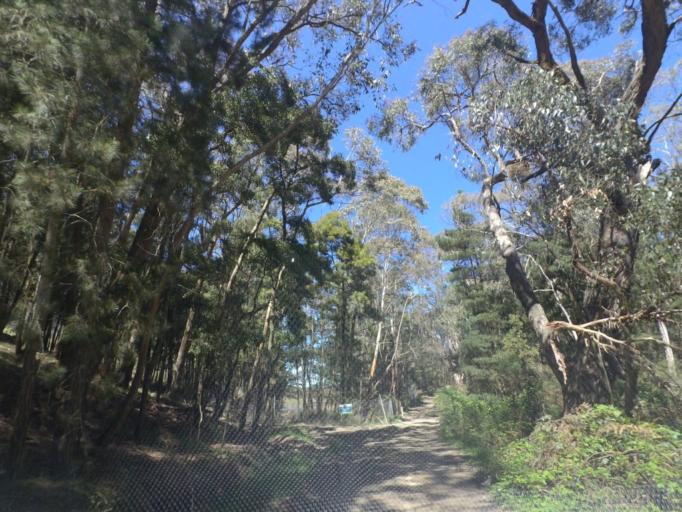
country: AU
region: Victoria
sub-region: Hume
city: Sunbury
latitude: -37.3902
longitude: 144.5531
